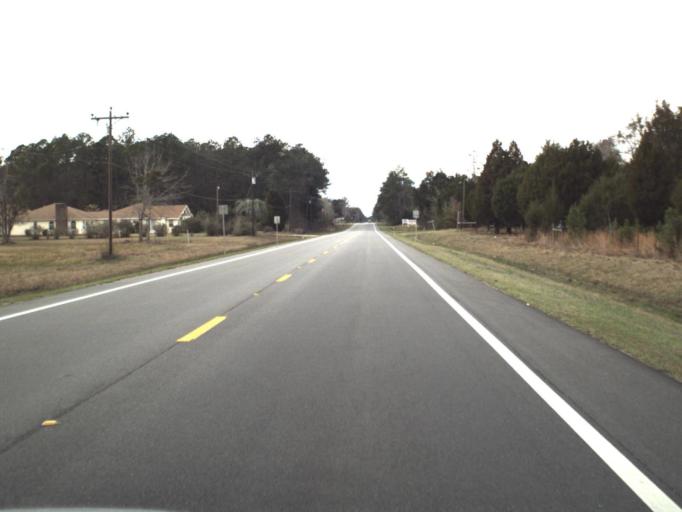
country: US
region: Florida
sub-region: Gulf County
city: Wewahitchka
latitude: 30.1205
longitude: -85.2137
